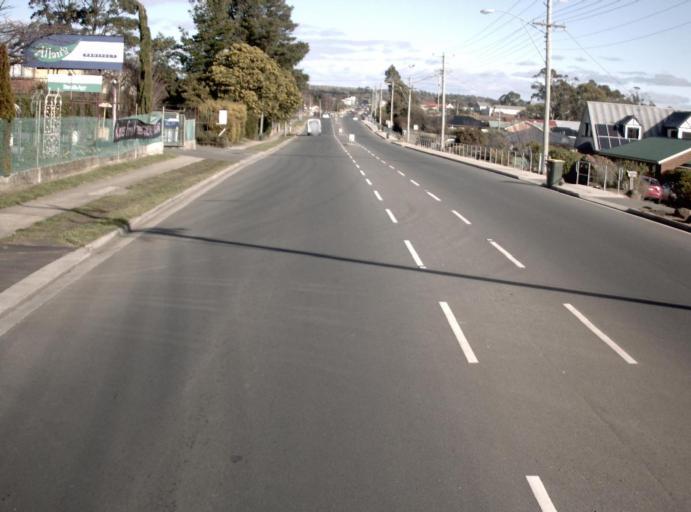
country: AU
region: Tasmania
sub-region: Launceston
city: Summerhill
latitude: -41.4750
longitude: 147.1277
